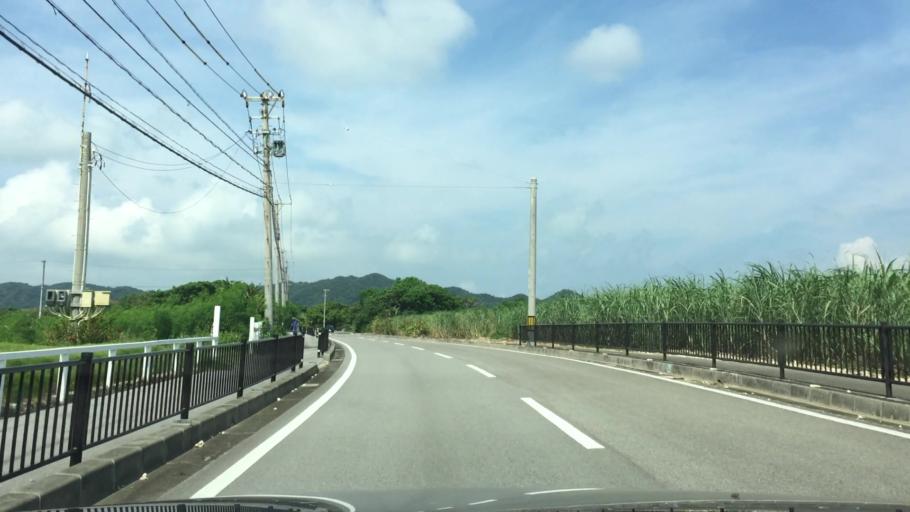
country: JP
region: Okinawa
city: Ishigaki
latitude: 24.4987
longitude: 124.2415
